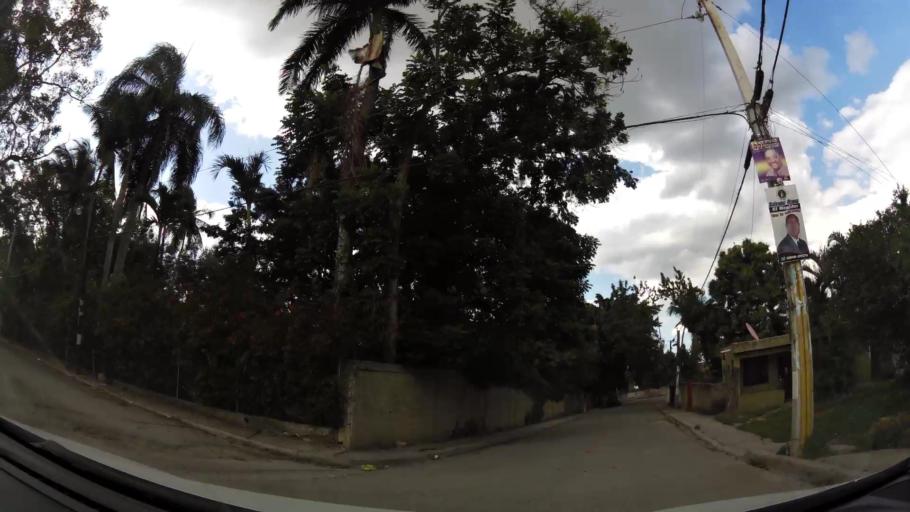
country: DO
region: Nacional
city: Ensanche Luperon
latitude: 18.5563
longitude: -69.8976
